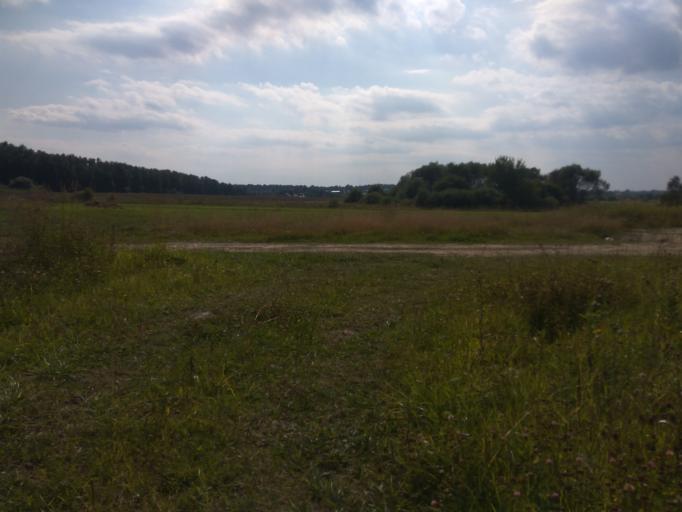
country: RU
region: Moskovskaya
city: Kubinka
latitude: 55.5835
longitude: 36.7427
